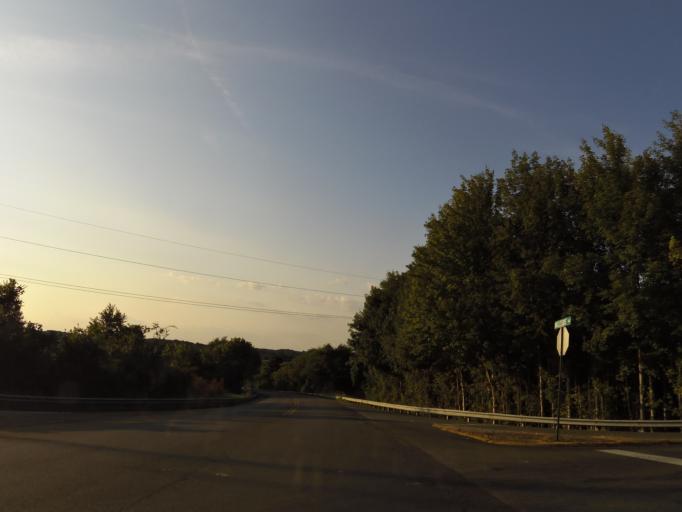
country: US
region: Tennessee
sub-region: McMinn County
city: Athens
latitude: 35.4760
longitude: -84.5886
